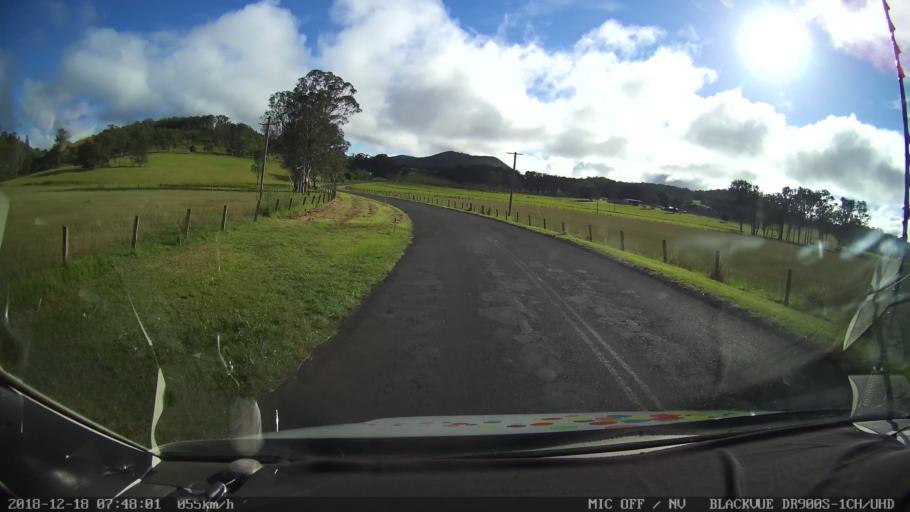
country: AU
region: New South Wales
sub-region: Kyogle
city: Kyogle
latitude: -28.4614
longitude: 152.5620
